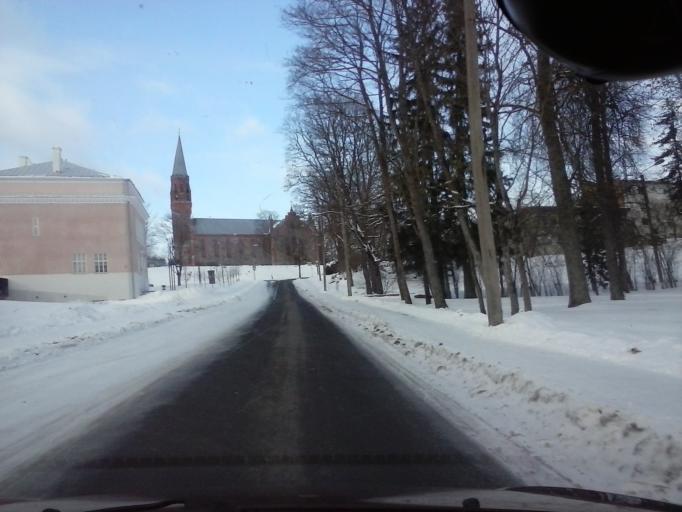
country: EE
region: Viljandimaa
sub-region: Viljandi linn
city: Viljandi
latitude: 58.3619
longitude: 25.5916
